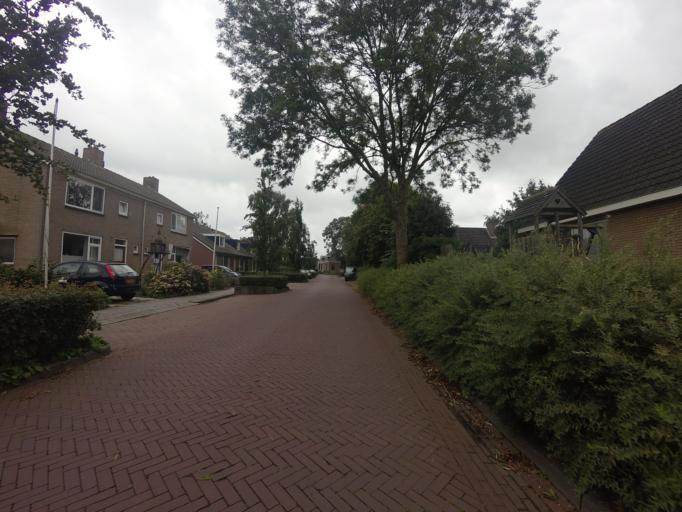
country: NL
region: Friesland
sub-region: Sudwest Fryslan
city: Heeg
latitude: 52.9947
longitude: 5.5485
